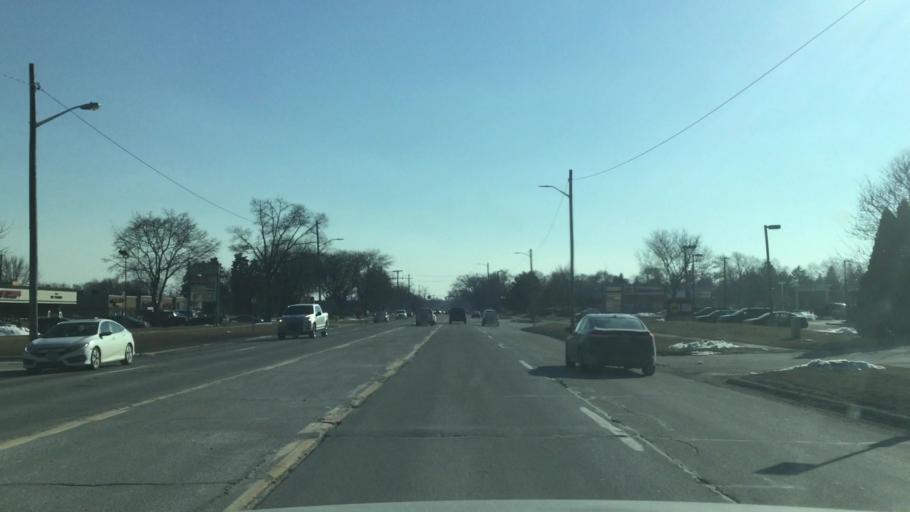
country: US
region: Michigan
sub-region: Wayne County
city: Westland
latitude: 42.3341
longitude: -83.3855
